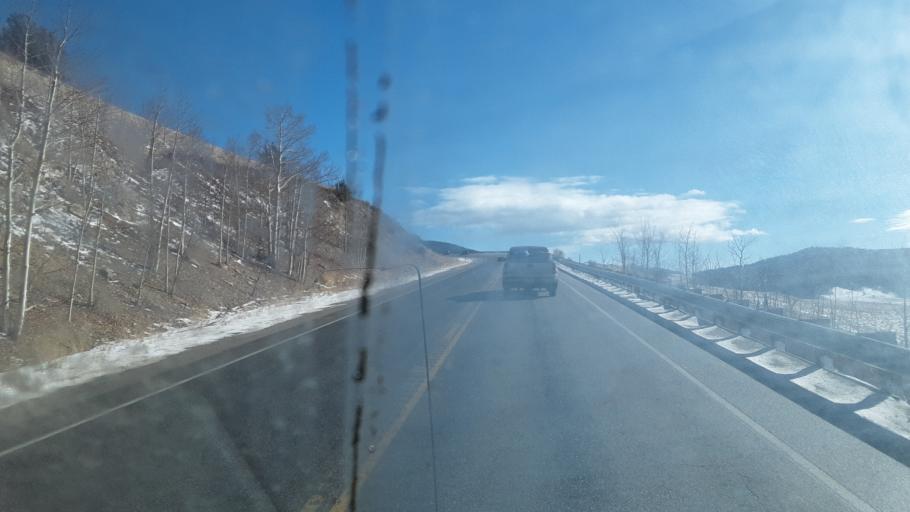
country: US
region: Colorado
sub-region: Summit County
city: Breckenridge
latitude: 39.4032
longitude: -105.7645
